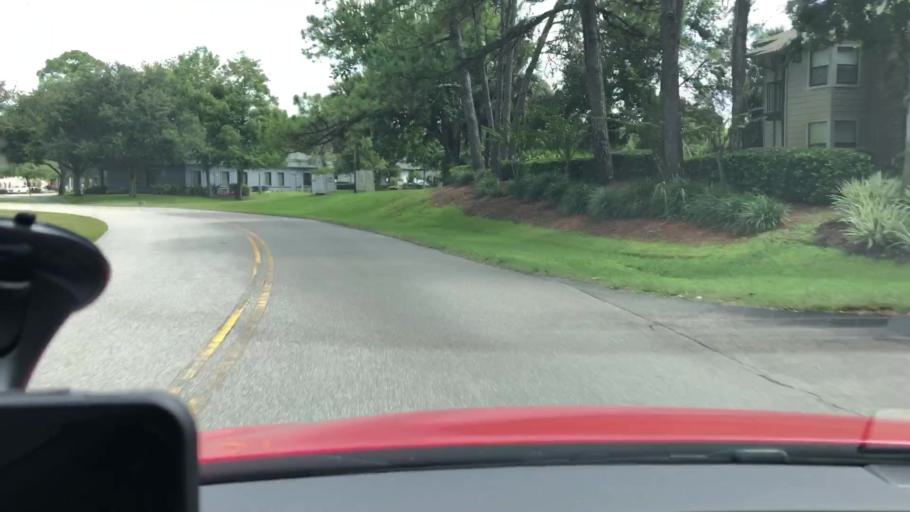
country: US
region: Florida
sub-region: Volusia County
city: Port Orange
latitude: 29.1246
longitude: -81.0143
